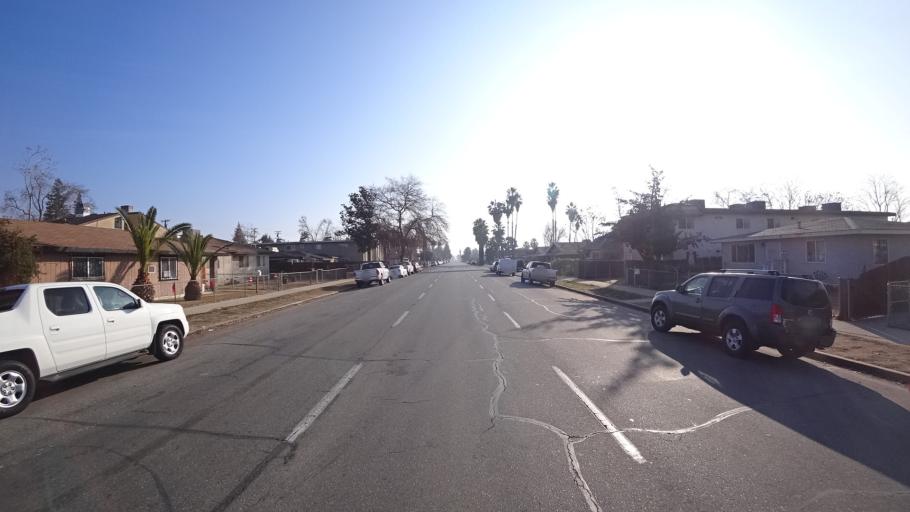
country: US
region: California
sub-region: Kern County
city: Bakersfield
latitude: 35.3823
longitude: -118.9971
